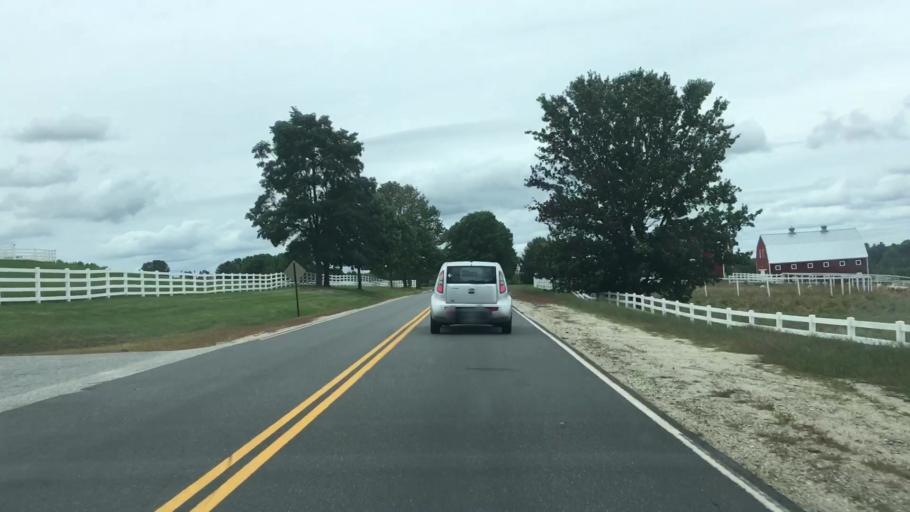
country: US
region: Maine
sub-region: Cumberland County
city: New Gloucester
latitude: 43.8932
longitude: -70.2539
